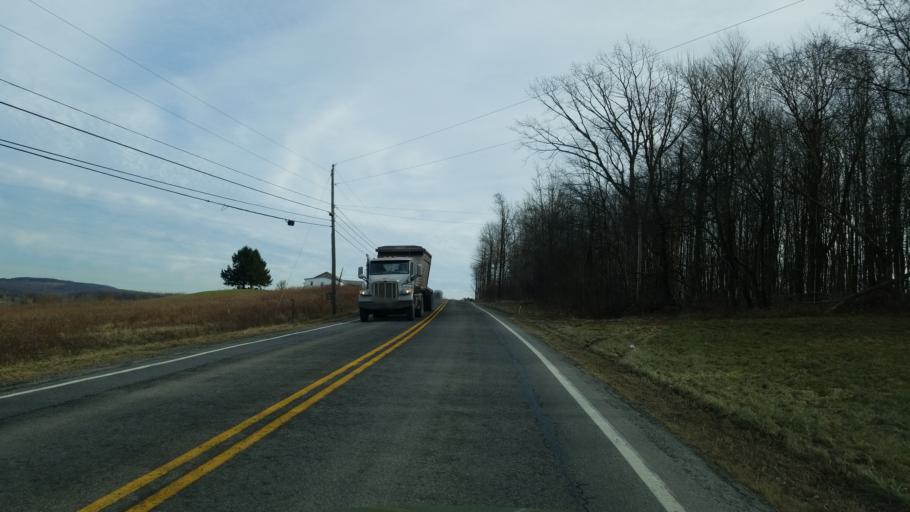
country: US
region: Pennsylvania
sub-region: Indiana County
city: Johnsonburg
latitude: 40.9157
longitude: -78.8413
